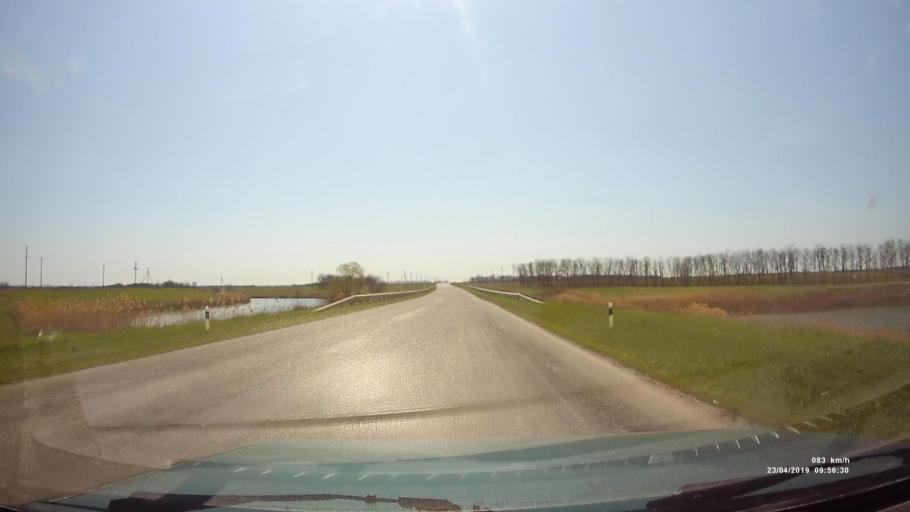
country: RU
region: Rostov
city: Orlovskiy
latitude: 46.7975
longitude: 42.0727
